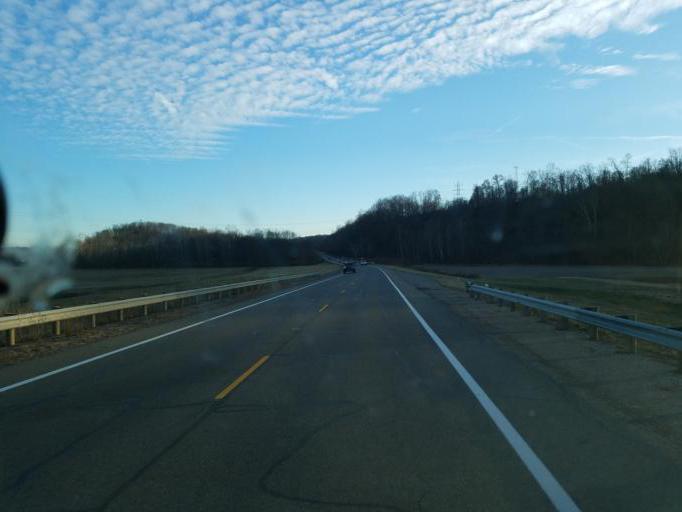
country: US
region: Ohio
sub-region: Muskingum County
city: Dresden
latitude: 40.1362
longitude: -82.0277
